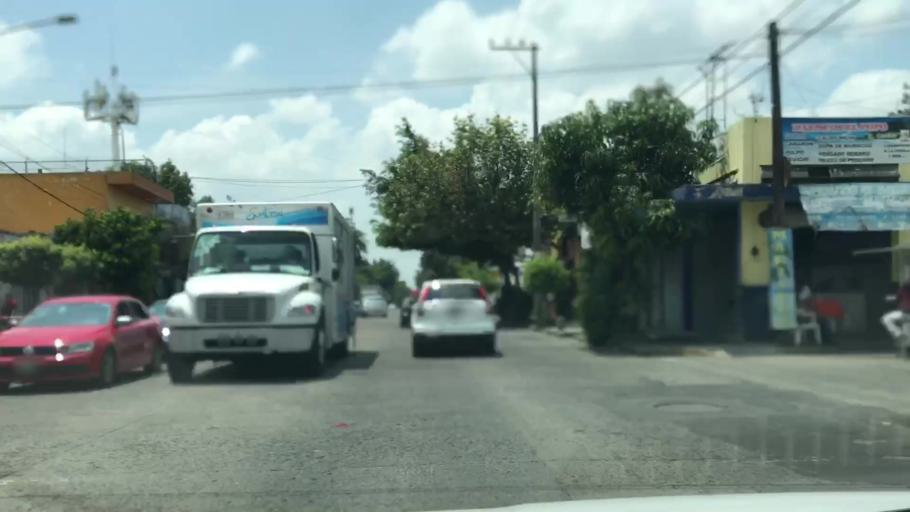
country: MX
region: Jalisco
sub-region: Zapopan
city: Zapopan
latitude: 20.6965
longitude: -103.3581
